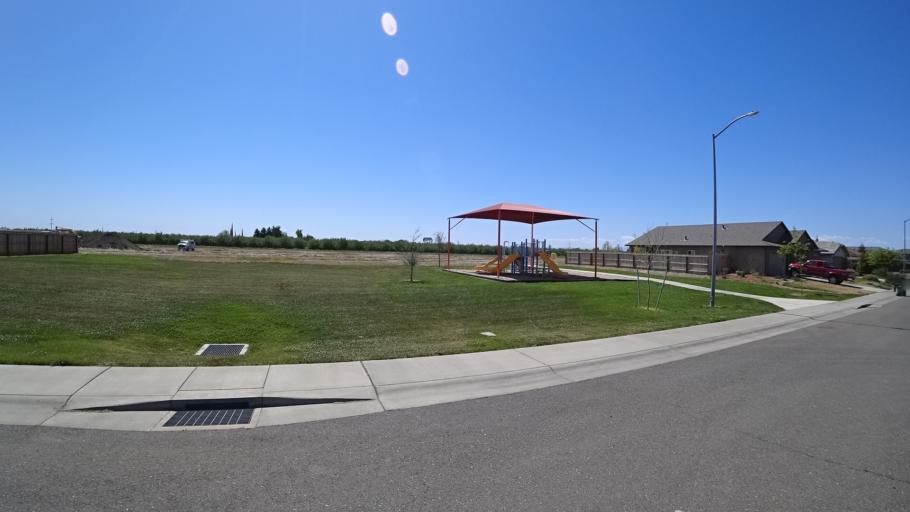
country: US
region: California
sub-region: Glenn County
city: Orland
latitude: 39.7449
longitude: -122.1711
